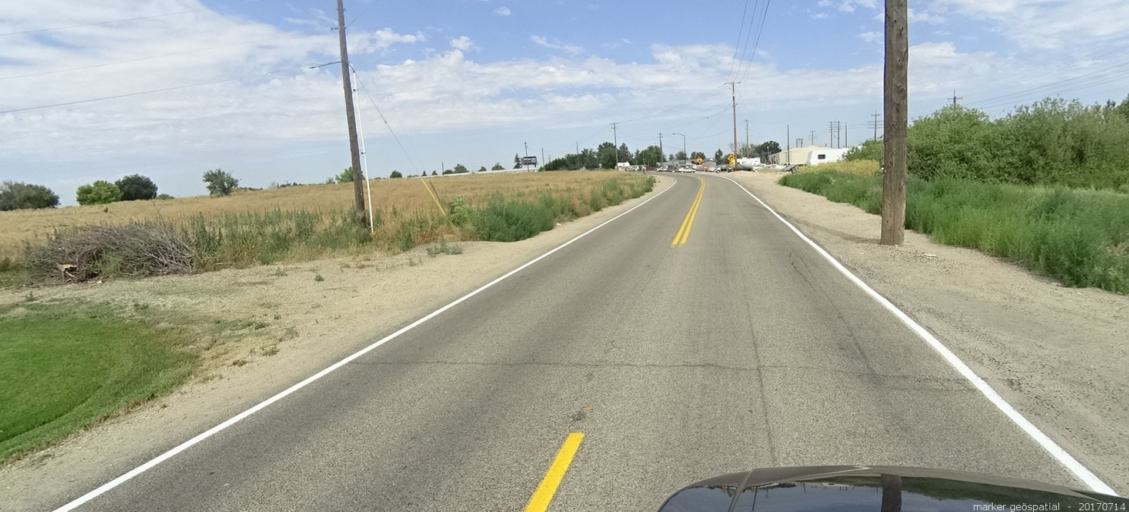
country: US
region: Idaho
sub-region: Ada County
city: Kuna
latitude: 43.4880
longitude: -116.4189
